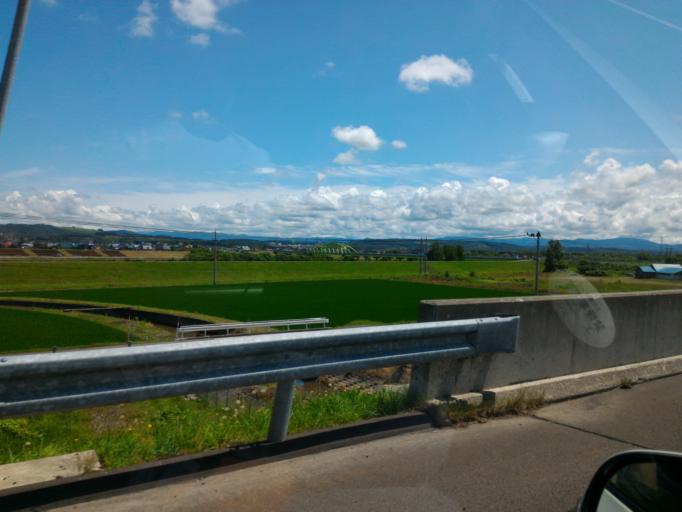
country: JP
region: Hokkaido
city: Nayoro
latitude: 44.3492
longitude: 142.4358
